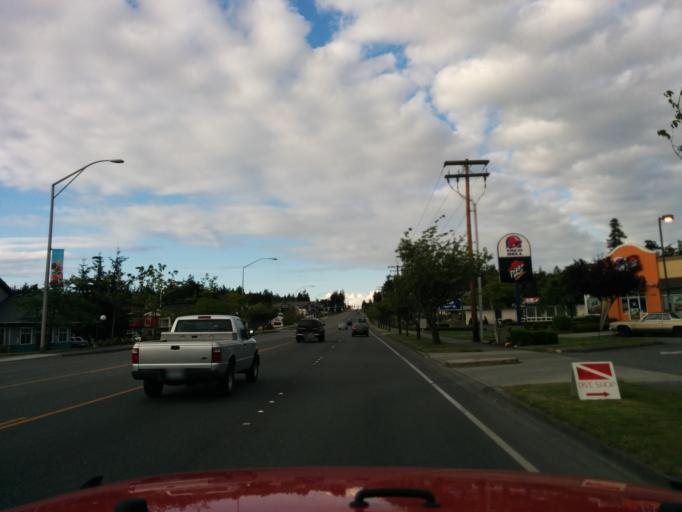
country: US
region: Washington
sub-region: Island County
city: Oak Harbor
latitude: 48.3042
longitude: -122.6460
